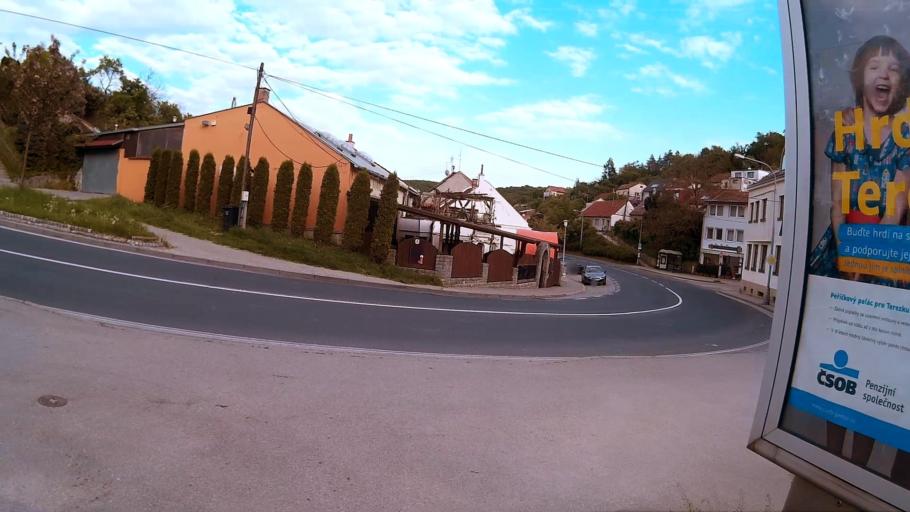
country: CZ
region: South Moravian
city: Ostopovice
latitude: 49.1921
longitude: 16.5387
